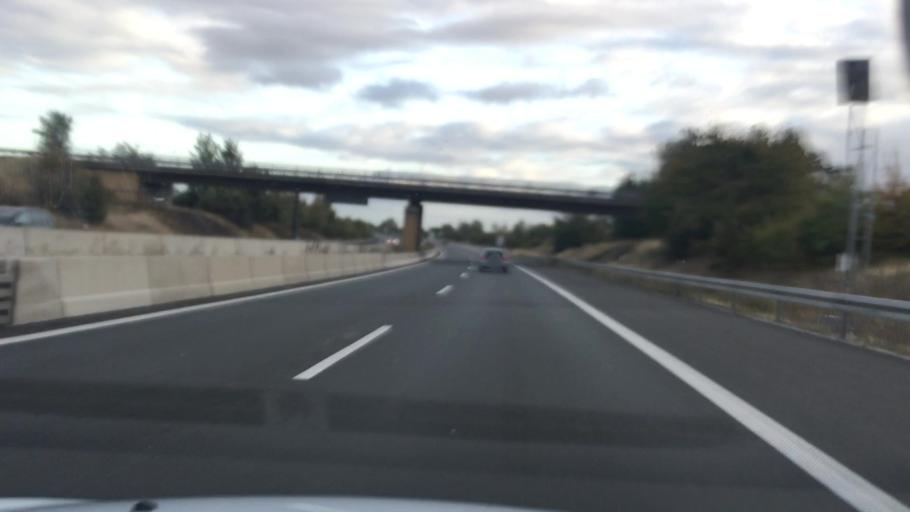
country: DE
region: Saxony-Anhalt
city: Plotzkau
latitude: 51.7348
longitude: 11.6677
